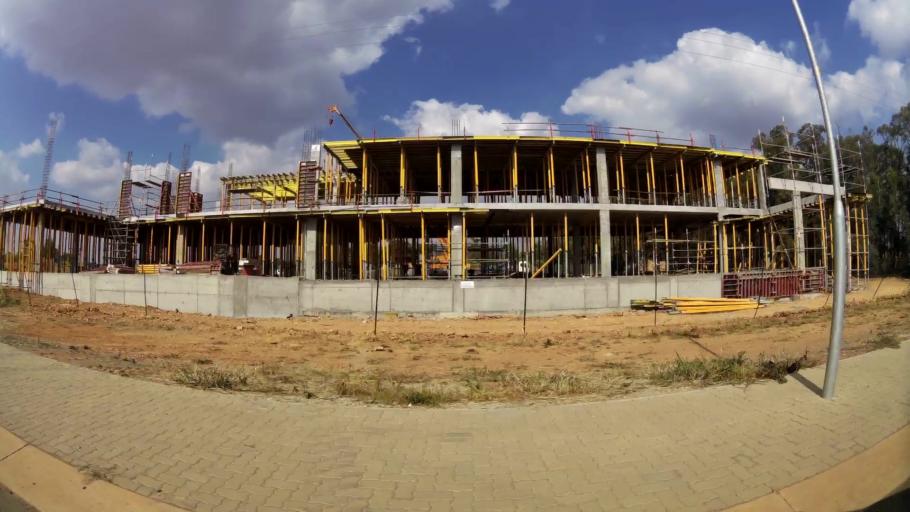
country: ZA
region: Gauteng
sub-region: City of Tshwane Metropolitan Municipality
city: Centurion
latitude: -25.8101
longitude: 28.3462
